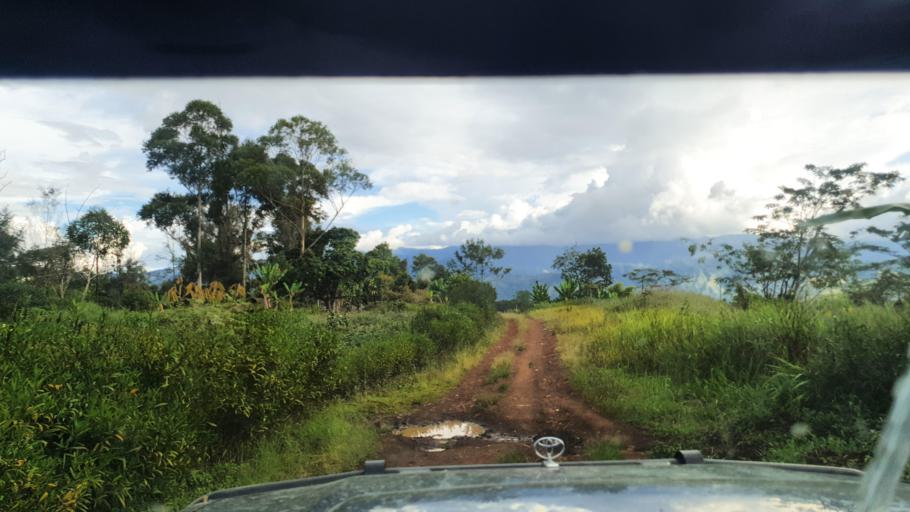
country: PG
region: Jiwaka
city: Minj
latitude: -5.9160
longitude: 144.8202
